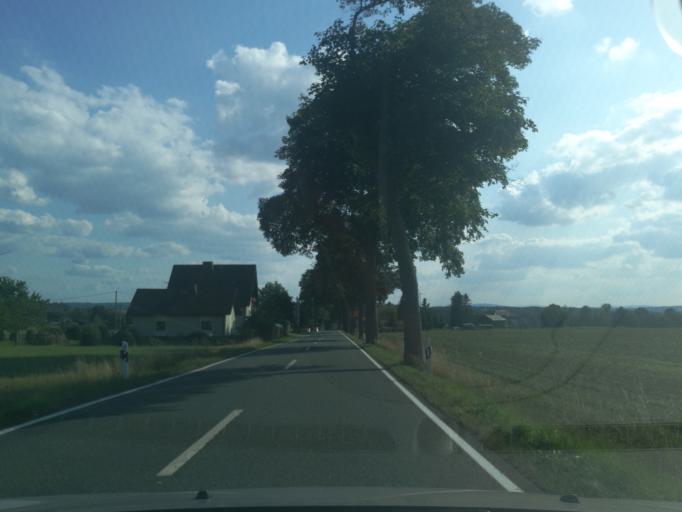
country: DE
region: Saxony
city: Eichigt
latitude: 50.3300
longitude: 12.1579
